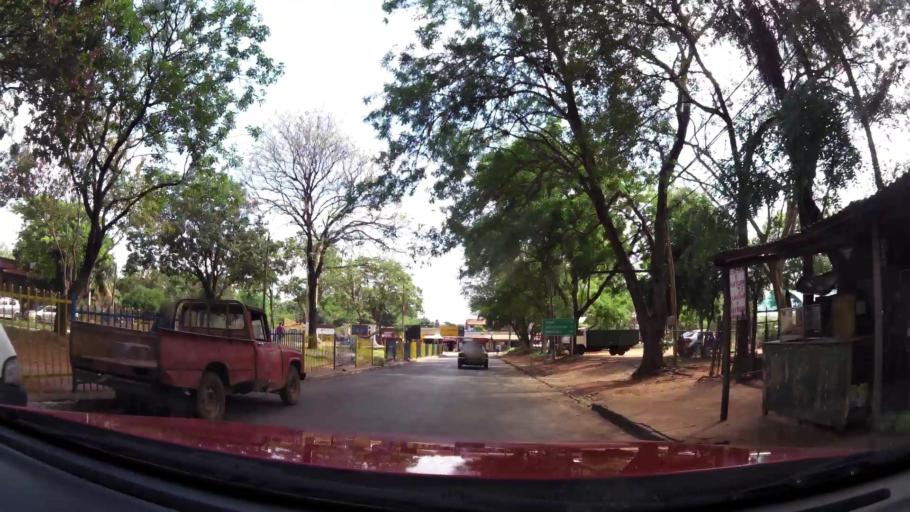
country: PY
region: Central
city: San Lorenzo
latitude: -25.2649
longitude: -57.4843
